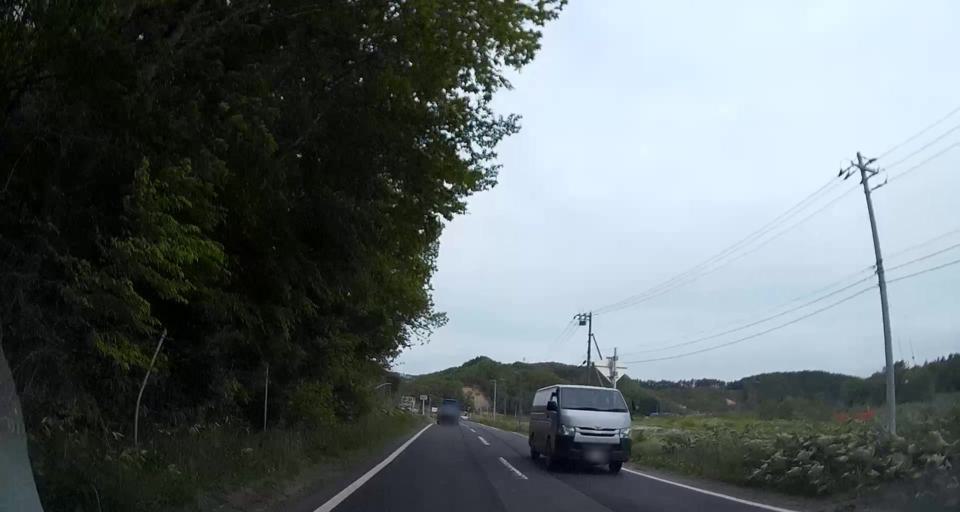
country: JP
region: Hokkaido
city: Chitose
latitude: 42.7539
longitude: 141.9158
